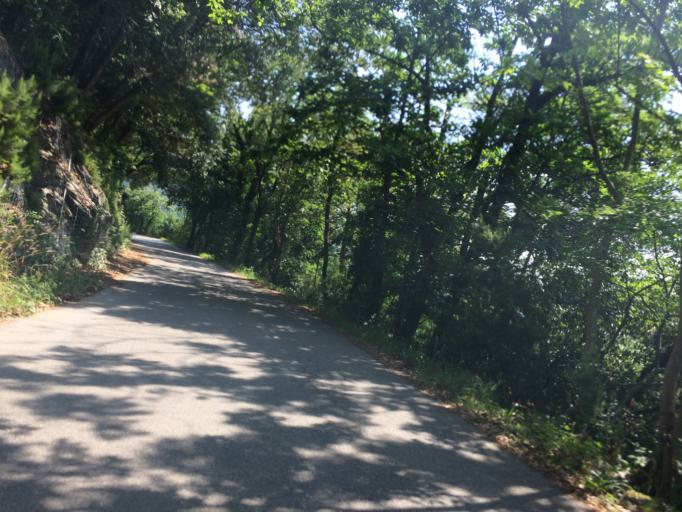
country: IT
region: Liguria
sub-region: Provincia di Savona
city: Varazze
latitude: 44.3970
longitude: 8.5754
